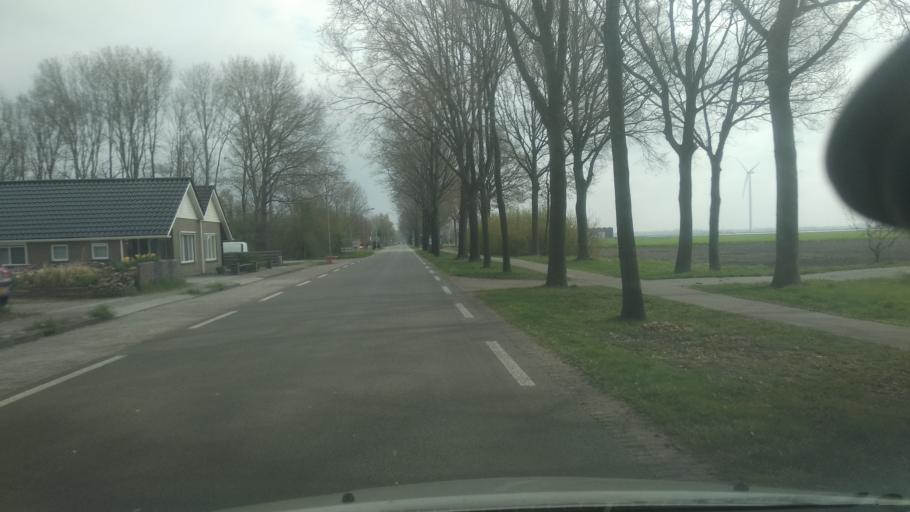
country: NL
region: Groningen
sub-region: Gemeente Stadskanaal
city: Stadskanaal
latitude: 52.9151
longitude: 6.9512
